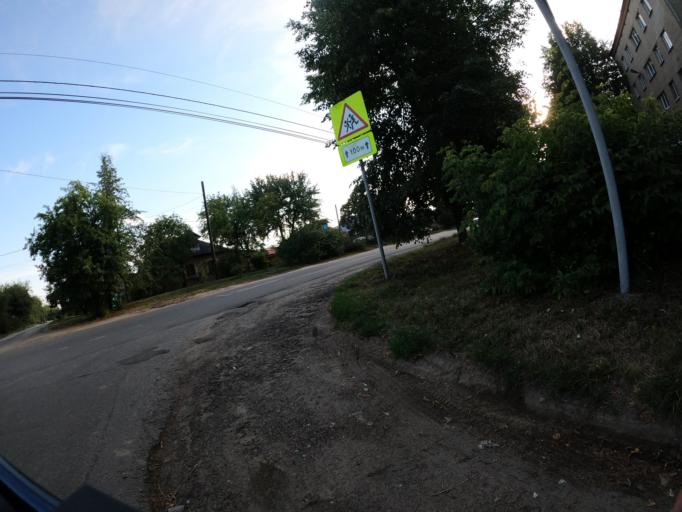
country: RU
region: Moskovskaya
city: Raduzhnyy
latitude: 55.1085
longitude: 38.7302
